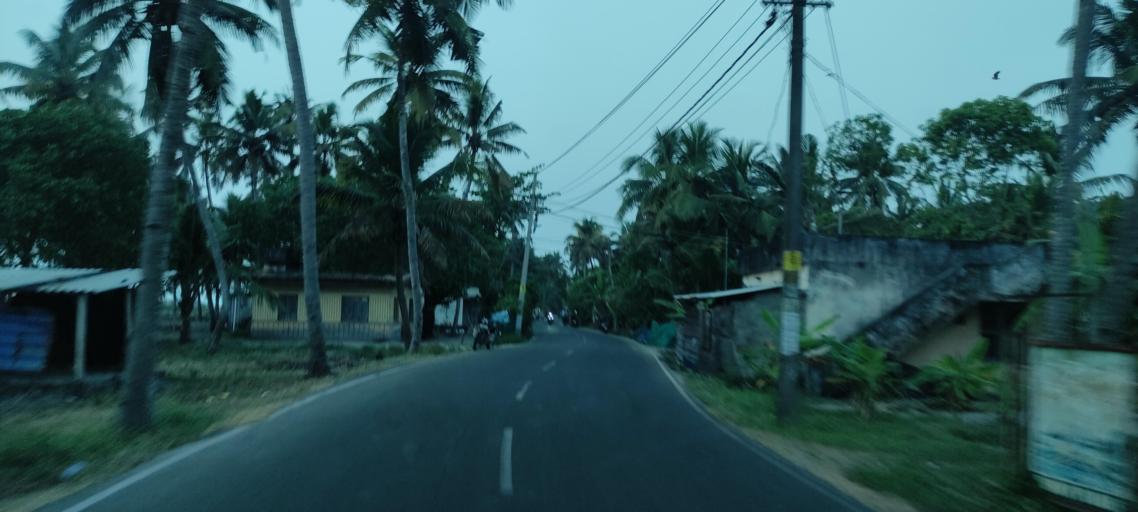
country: IN
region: Kerala
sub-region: Alappuzha
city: Kayankulam
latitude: 9.1225
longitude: 76.4697
